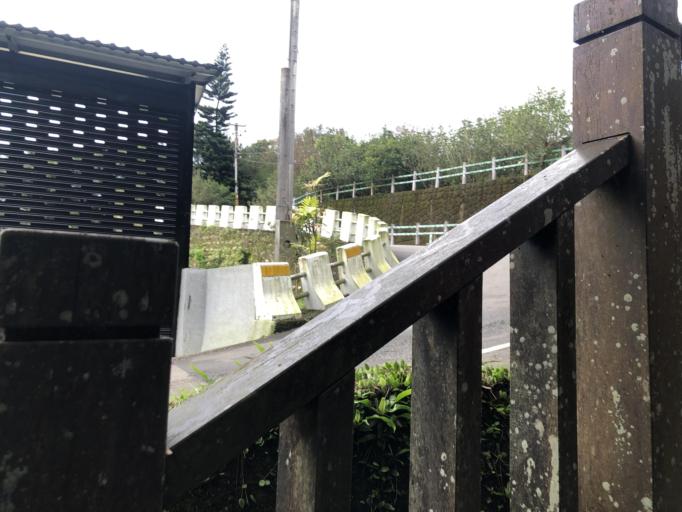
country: TW
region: Taipei
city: Taipei
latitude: 25.0255
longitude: 121.6605
